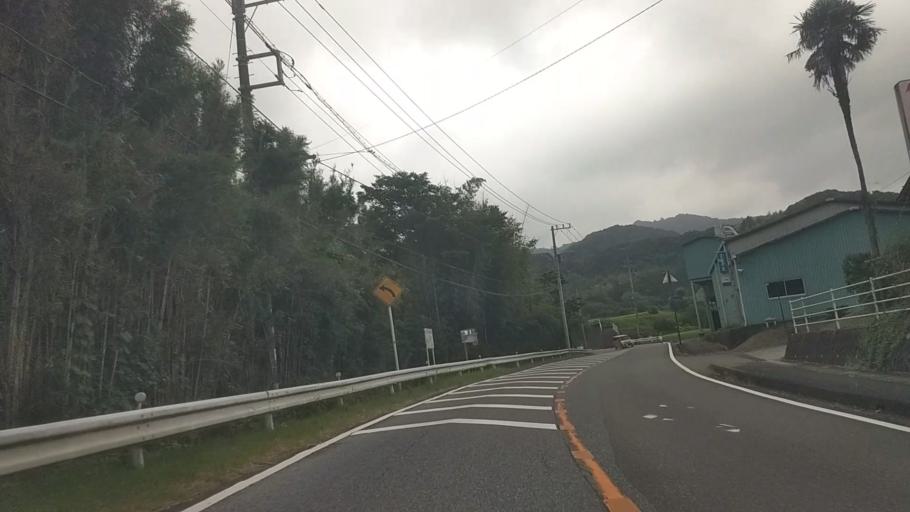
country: JP
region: Chiba
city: Kawaguchi
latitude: 35.1392
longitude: 139.9775
